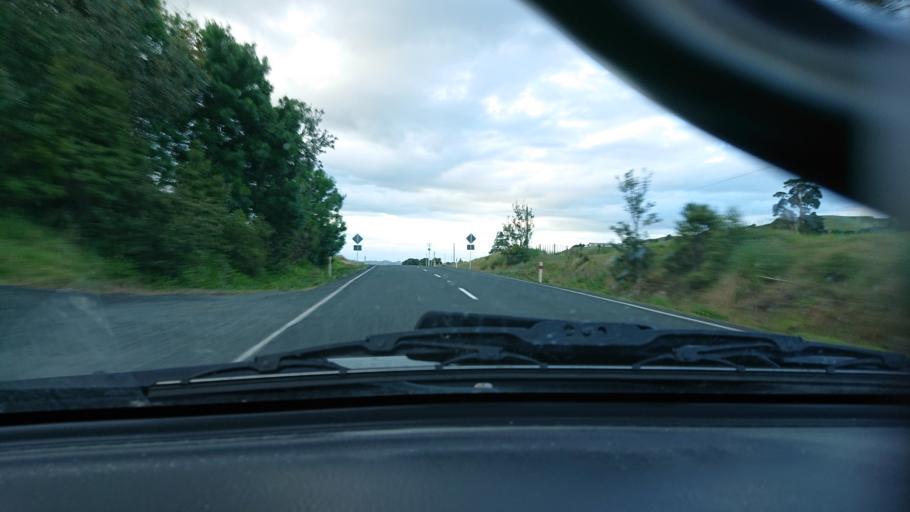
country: NZ
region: Auckland
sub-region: Auckland
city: Wellsford
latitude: -36.4542
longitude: 174.4354
